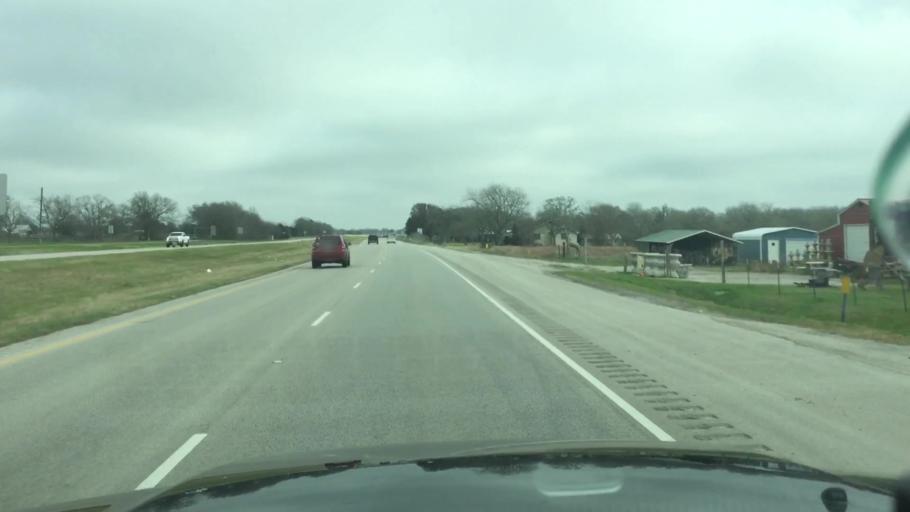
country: US
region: Texas
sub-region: Burleson County
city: Somerville
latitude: 30.1499
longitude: -96.6825
